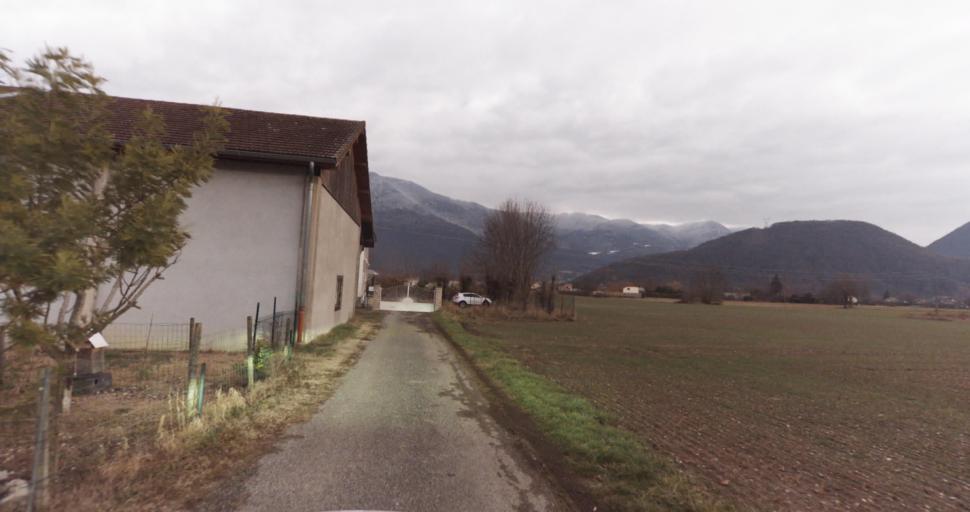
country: FR
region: Rhone-Alpes
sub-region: Departement de l'Isere
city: Vif
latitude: 45.0676
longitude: 5.6871
